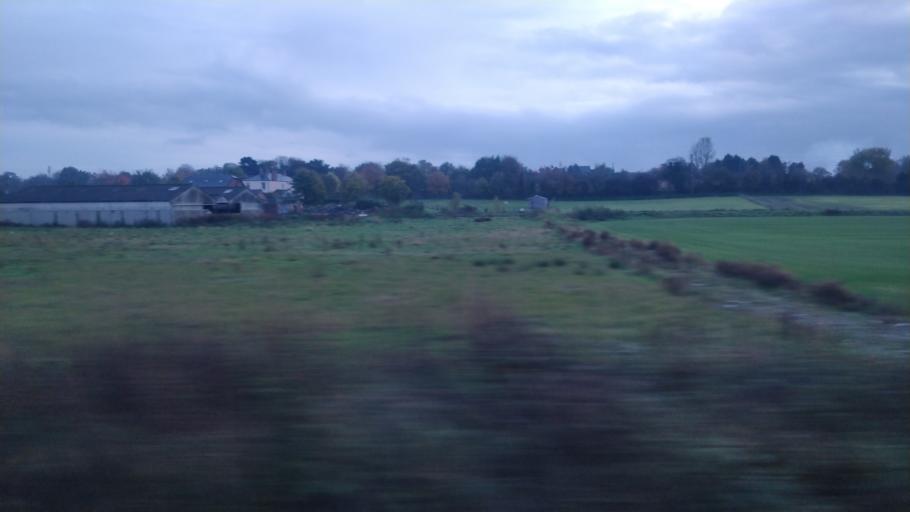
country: GB
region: England
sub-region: Lancashire
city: Parbold
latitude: 53.5935
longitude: -2.7838
